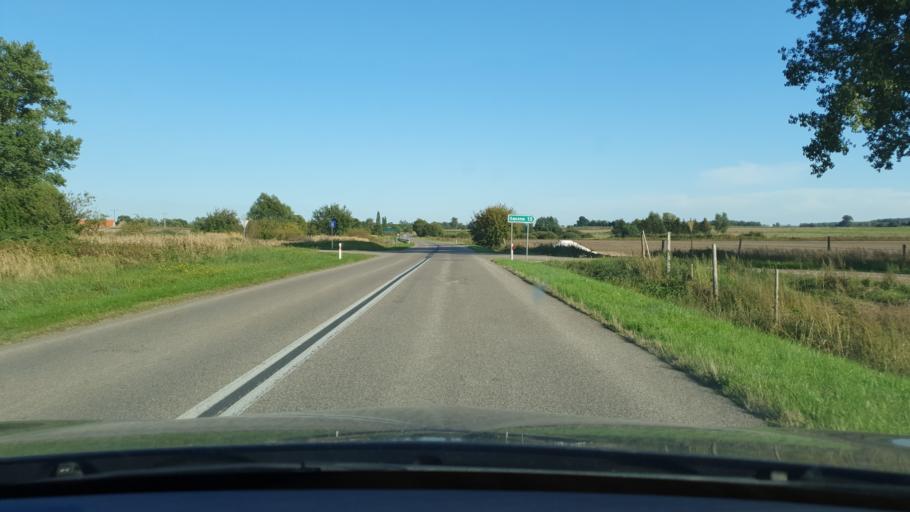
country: PL
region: West Pomeranian Voivodeship
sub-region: Powiat gryficki
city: Gryfice
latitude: 53.8163
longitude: 15.1592
